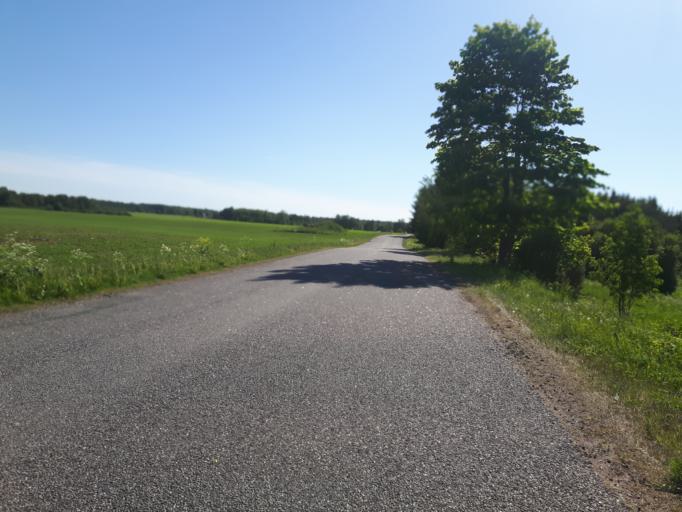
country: EE
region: Laeaene-Virumaa
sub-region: Haljala vald
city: Haljala
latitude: 59.5444
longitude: 26.1135
